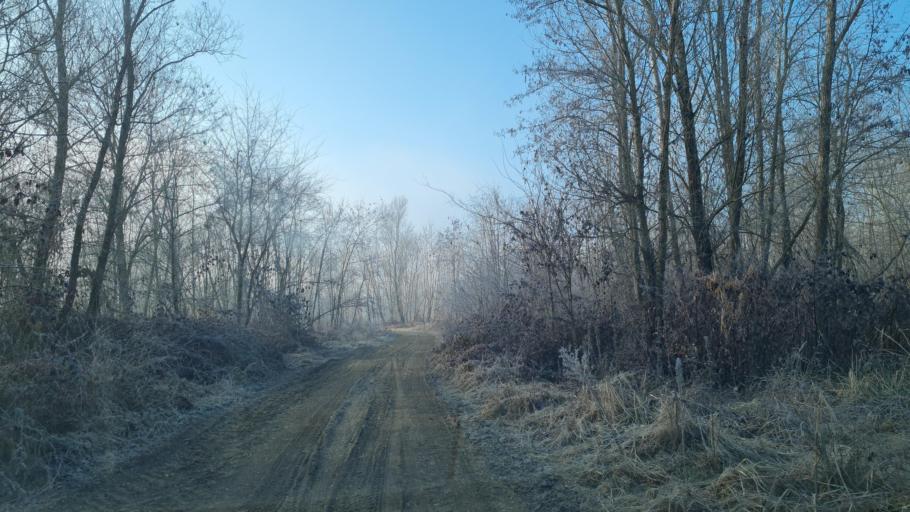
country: IT
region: Piedmont
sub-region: Provincia di Biella
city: Salussola
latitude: 45.4466
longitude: 8.1282
